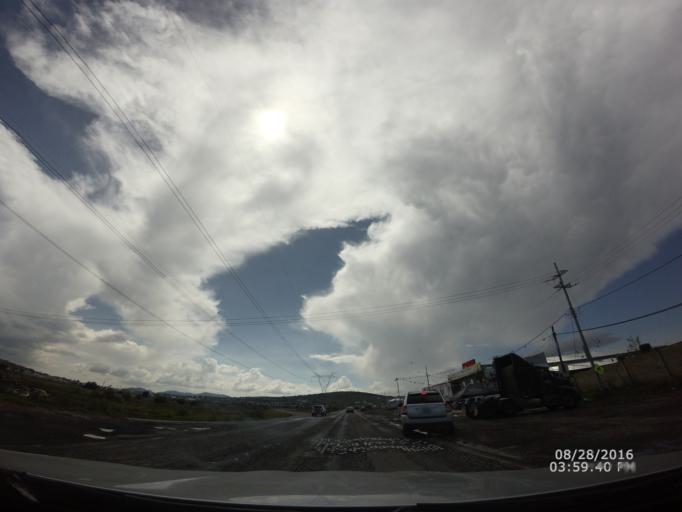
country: MX
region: Hidalgo
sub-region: Zempoala
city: Lindavista
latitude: 20.0385
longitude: -98.7867
